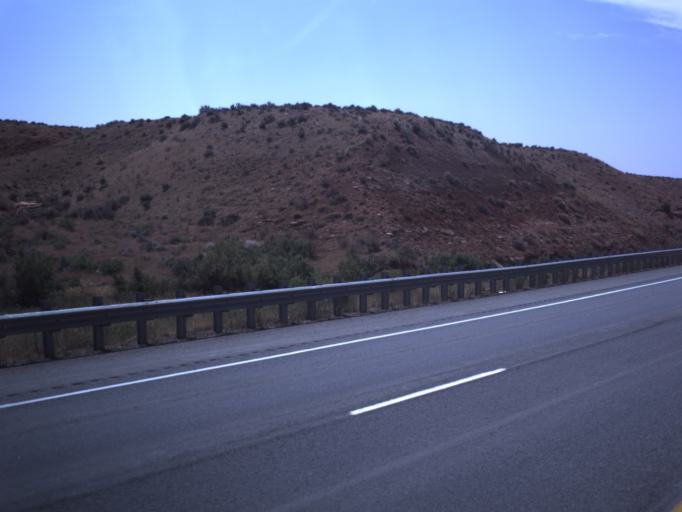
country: US
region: Utah
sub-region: Uintah County
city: Maeser
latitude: 40.3502
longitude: -109.6237
